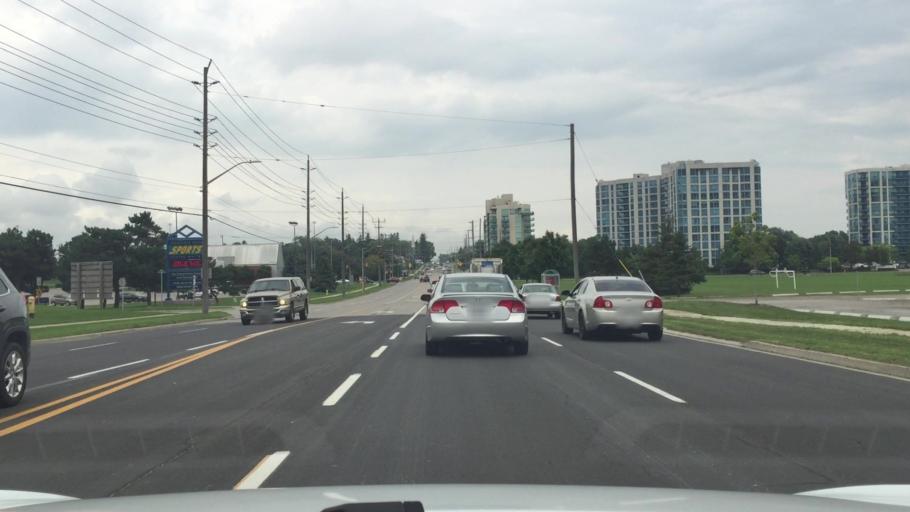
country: CA
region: Ontario
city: Ajax
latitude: 43.8605
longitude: -78.9428
